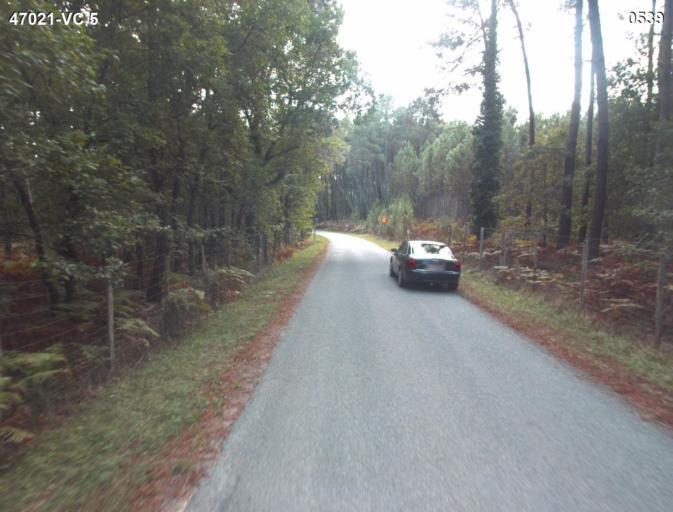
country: FR
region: Aquitaine
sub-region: Departement du Lot-et-Garonne
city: Barbaste
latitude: 44.1409
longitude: 0.2885
